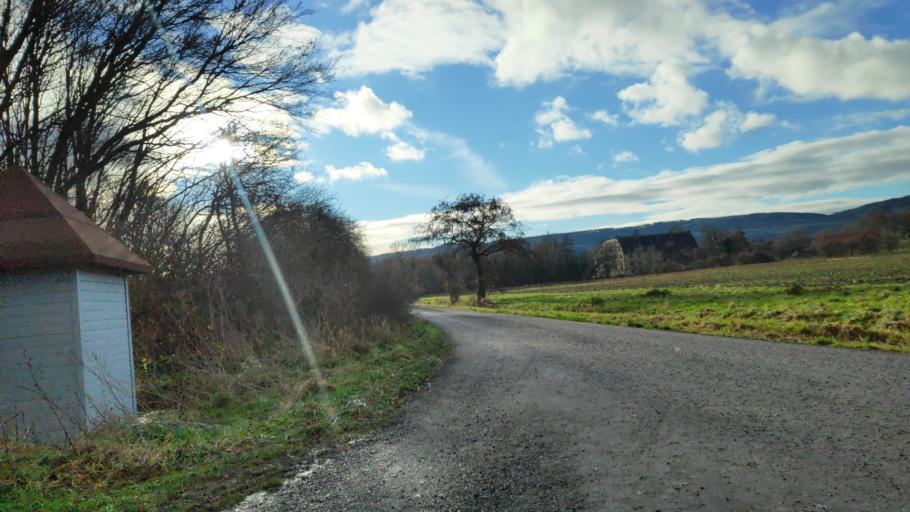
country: DE
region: North Rhine-Westphalia
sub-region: Regierungsbezirk Detmold
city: Minden
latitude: 52.2833
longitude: 8.8341
